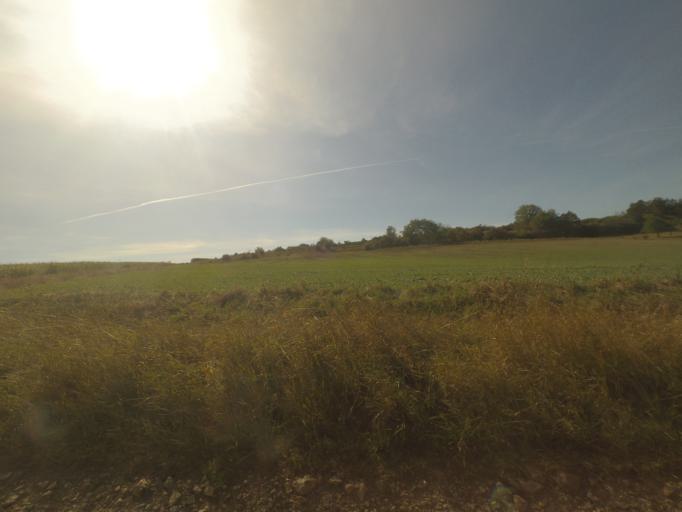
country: DE
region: Thuringia
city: Rottenbach
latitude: 50.7507
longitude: 11.1838
